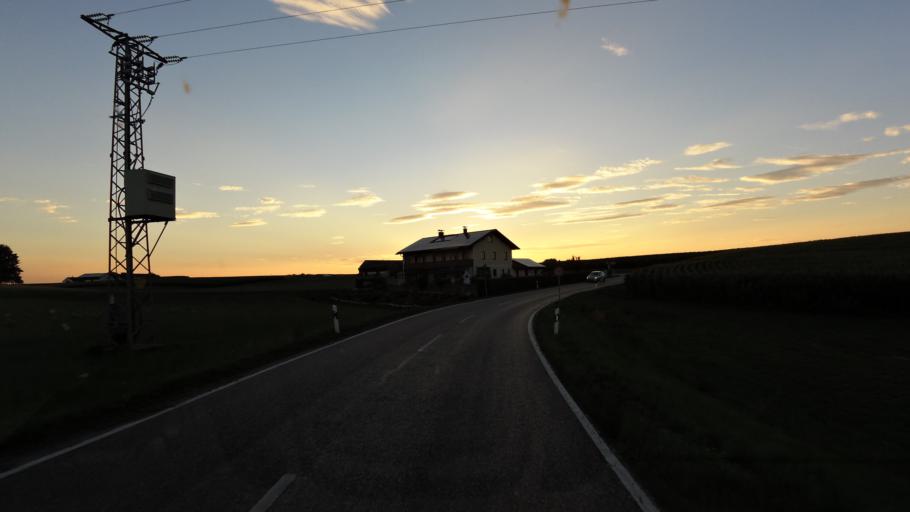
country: DE
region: Bavaria
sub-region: Upper Bavaria
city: Taufkirchen
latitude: 48.1109
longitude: 12.4703
